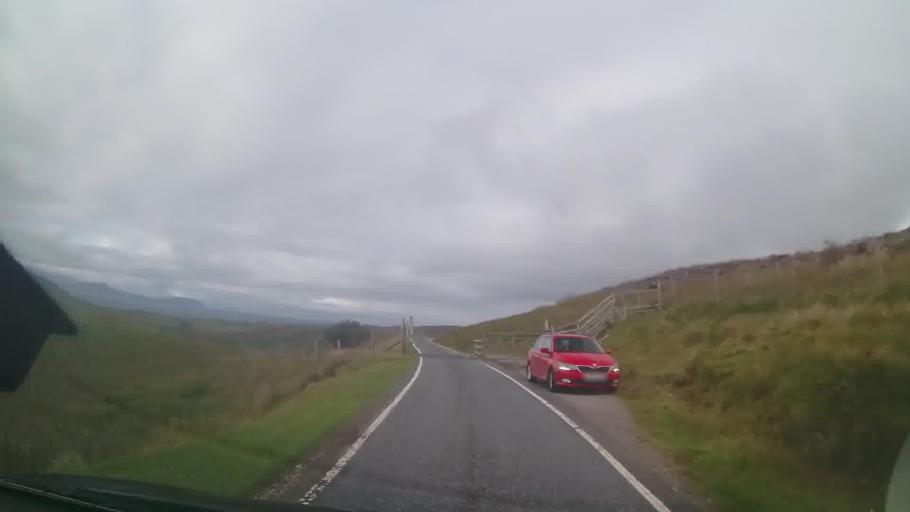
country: GB
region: Scotland
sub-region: Argyll and Bute
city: Isle Of Mull
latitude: 56.7267
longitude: -6.0373
